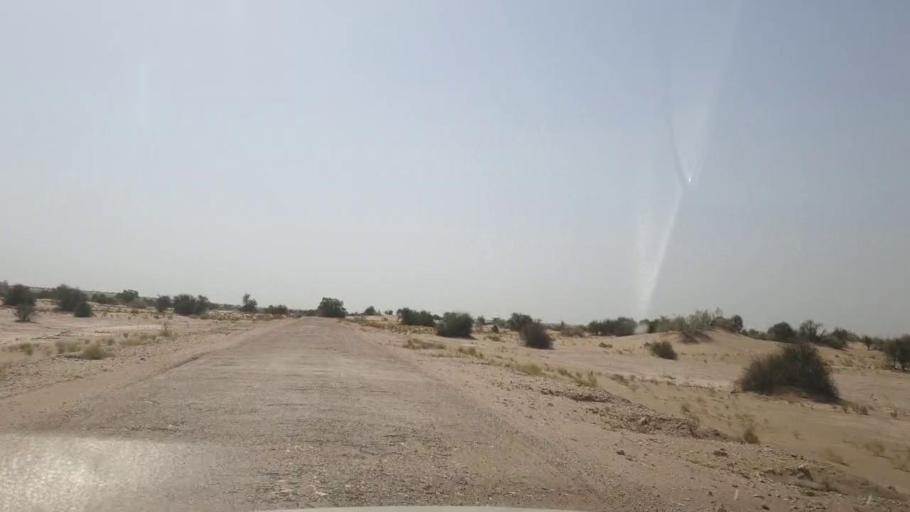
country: PK
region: Sindh
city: Khanpur
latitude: 27.4294
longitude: 69.2563
